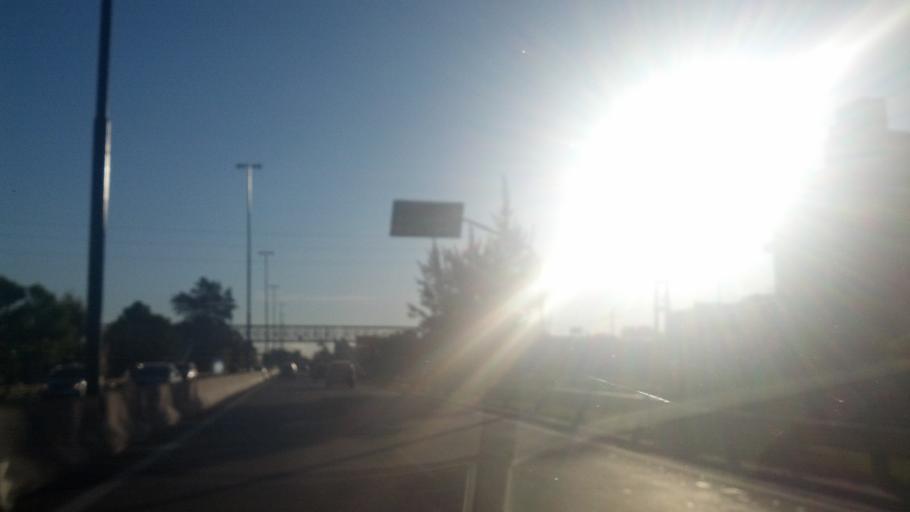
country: AR
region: Buenos Aires
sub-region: Partido de Lomas de Zamora
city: Lomas de Zamora
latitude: -34.7490
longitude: -58.4317
